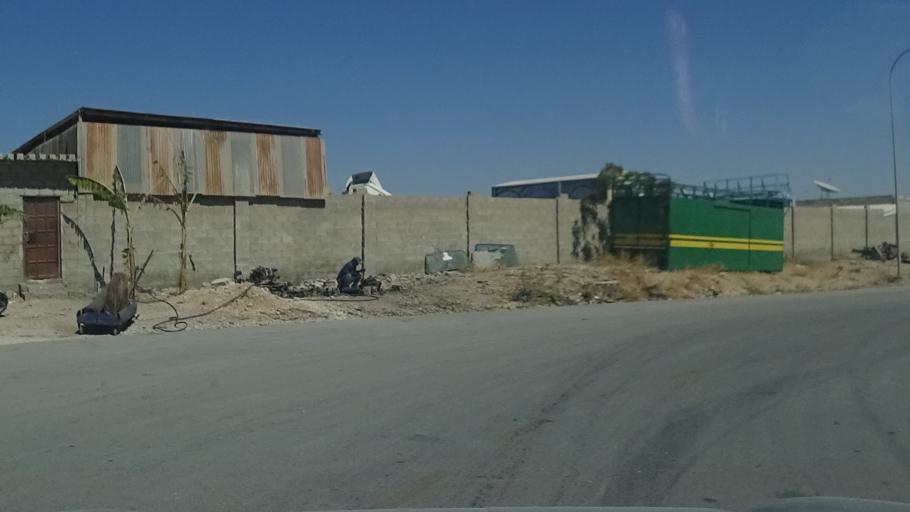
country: OM
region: Zufar
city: Salalah
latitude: 17.0331
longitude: 54.0392
